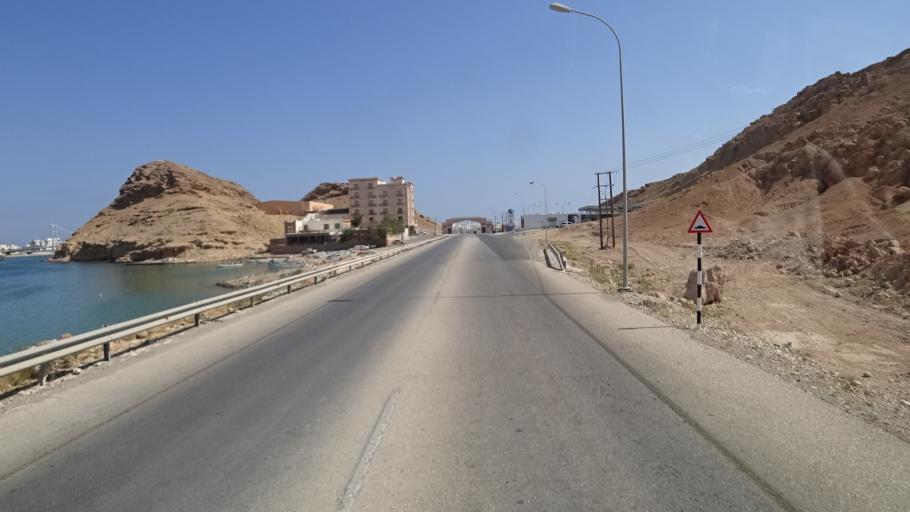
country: OM
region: Ash Sharqiyah
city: Sur
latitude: 22.5589
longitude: 59.5409
